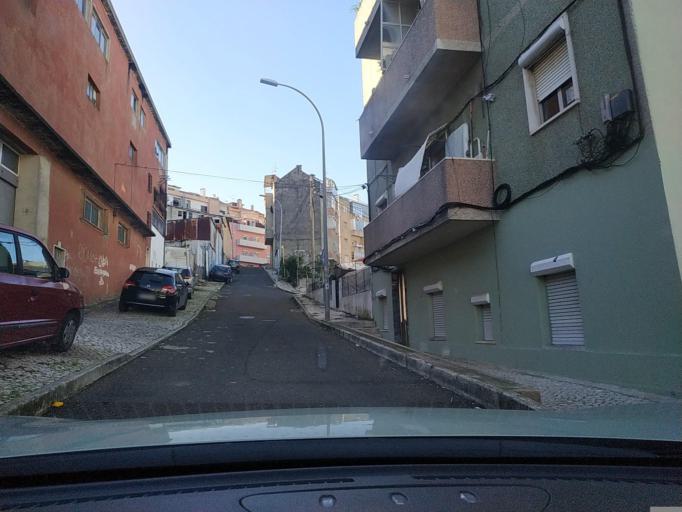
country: PT
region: Lisbon
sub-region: Odivelas
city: Pontinha
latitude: 38.7701
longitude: -9.2153
